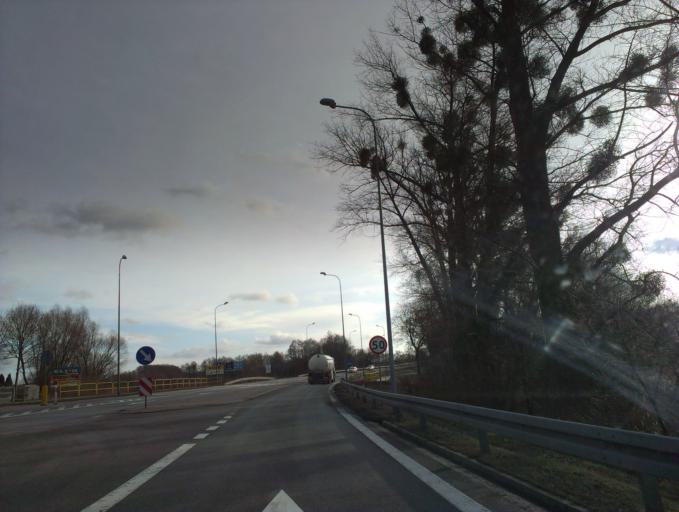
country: PL
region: Kujawsko-Pomorskie
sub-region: Powiat lipnowski
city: Kikol
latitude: 52.9094
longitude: 19.1196
